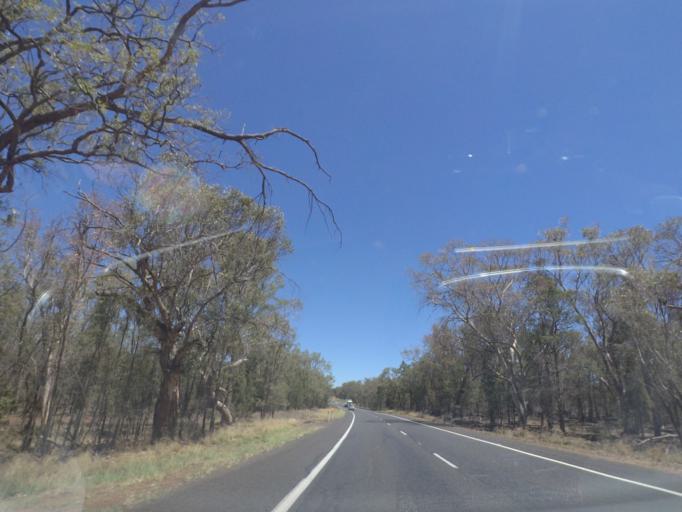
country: AU
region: New South Wales
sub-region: Warrumbungle Shire
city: Coonabarabran
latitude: -31.3444
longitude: 149.2964
